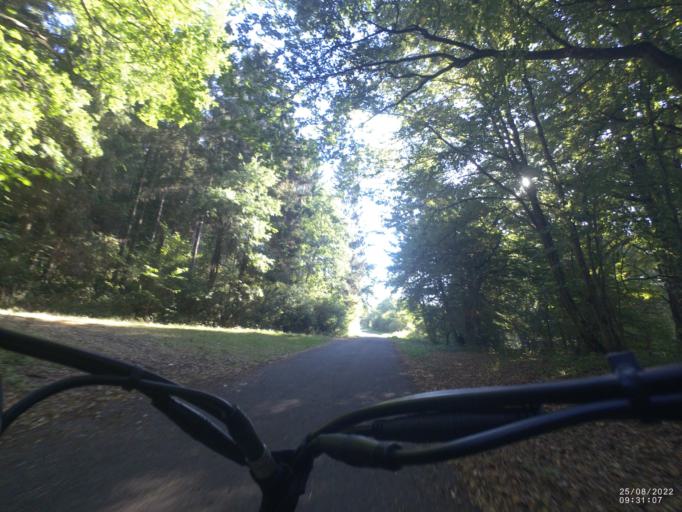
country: DE
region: Rheinland-Pfalz
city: Dohm-Lammersdorf
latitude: 50.2708
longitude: 6.6744
